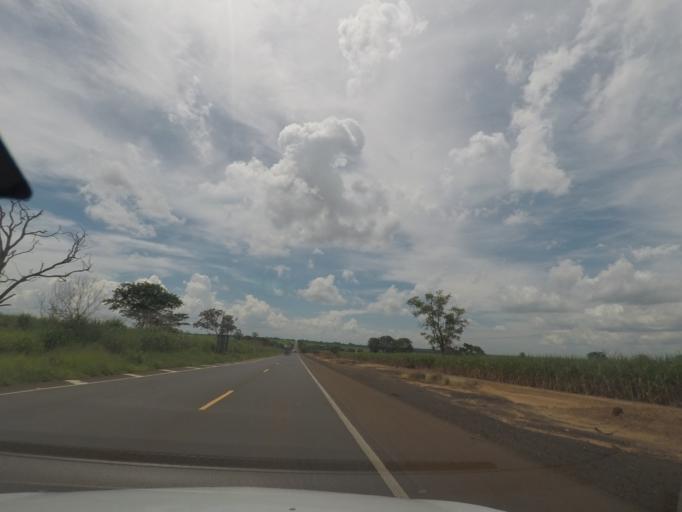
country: BR
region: Sao Paulo
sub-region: Barretos
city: Barretos
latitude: -20.3759
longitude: -48.6440
